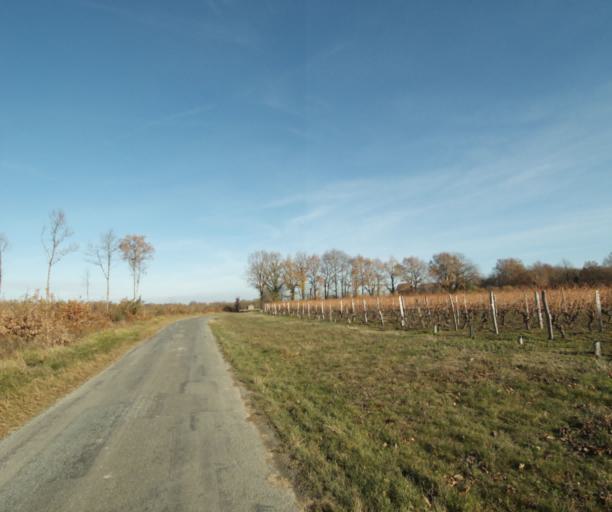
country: FR
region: Poitou-Charentes
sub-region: Departement de la Charente-Maritime
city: Chaniers
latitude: 45.7570
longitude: -0.5117
